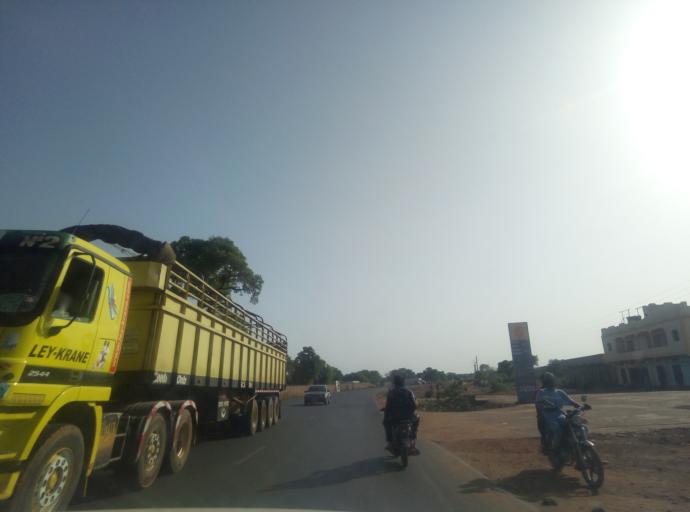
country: ML
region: Bamako
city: Bamako
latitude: 12.5825
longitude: -7.7737
